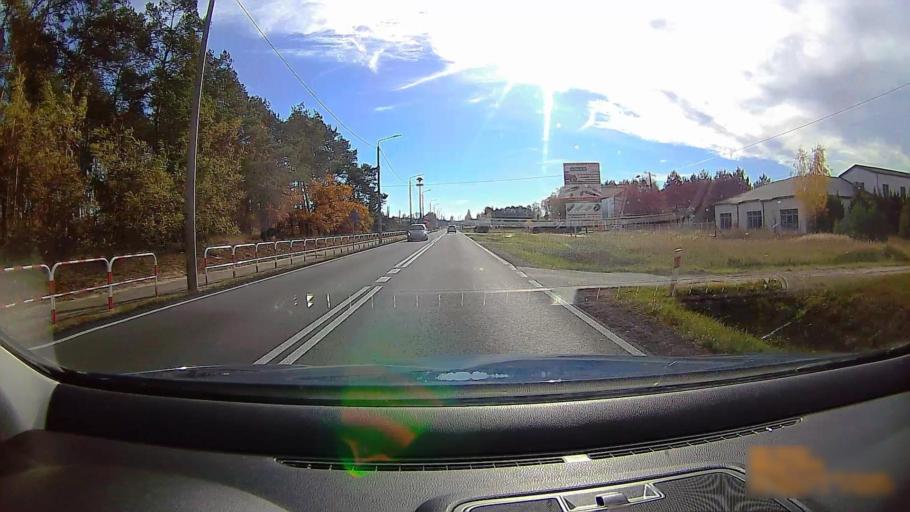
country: PL
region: Greater Poland Voivodeship
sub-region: Powiat ostrzeszowski
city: Ostrzeszow
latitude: 51.4467
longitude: 17.9105
